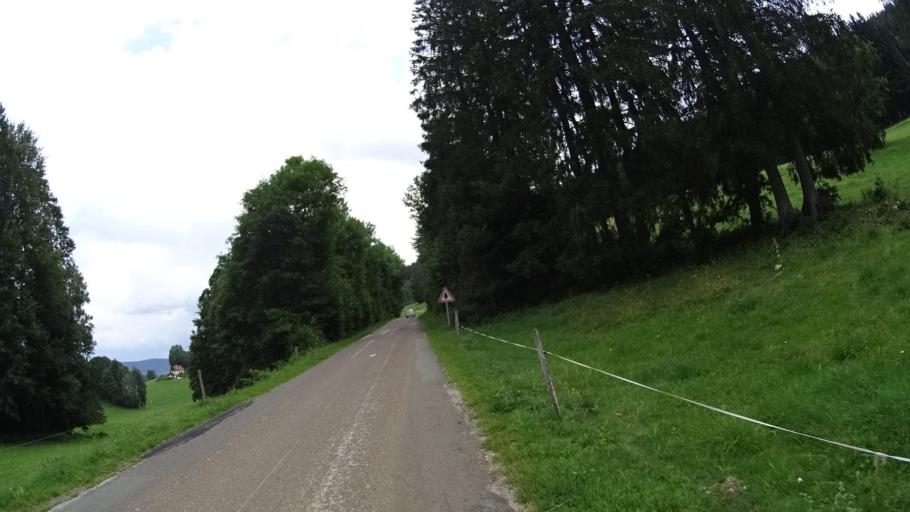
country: FR
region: Franche-Comte
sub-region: Departement du Doubs
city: Les Fourgs
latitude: 46.8181
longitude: 6.3315
